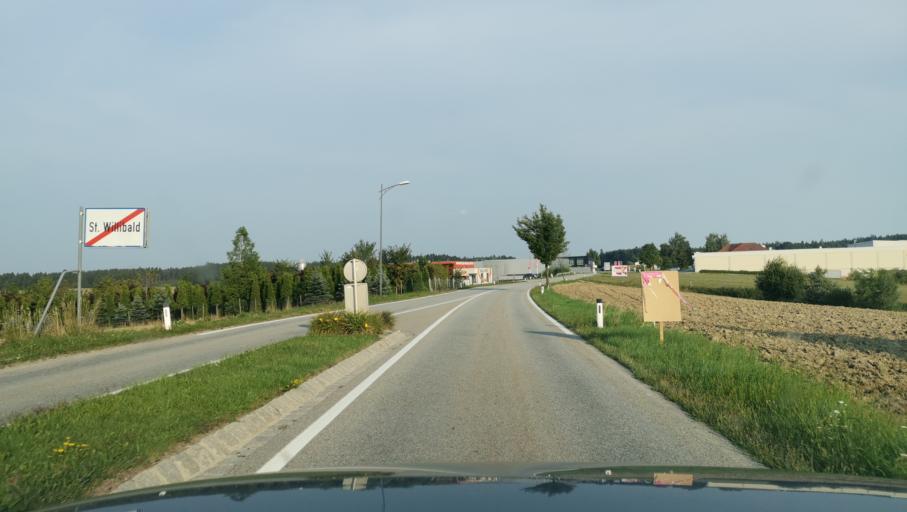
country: AT
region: Upper Austria
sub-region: Politischer Bezirk Grieskirchen
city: Grieskirchen
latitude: 48.3593
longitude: 13.6939
